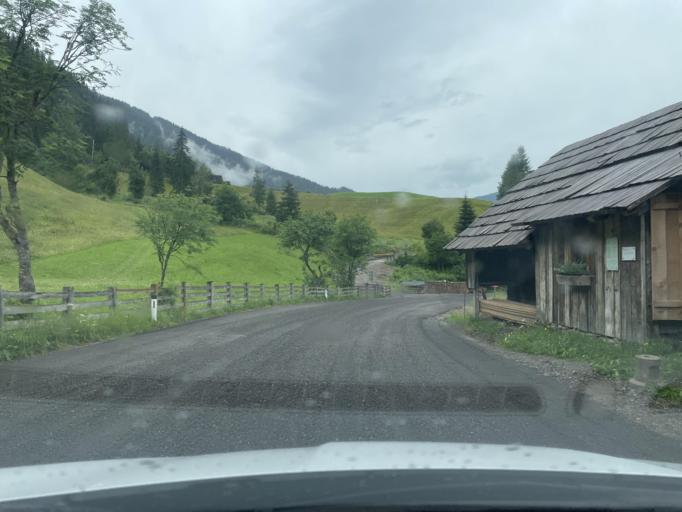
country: AT
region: Tyrol
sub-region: Politischer Bezirk Lienz
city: Ausservillgraten
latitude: 46.8008
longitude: 12.4509
